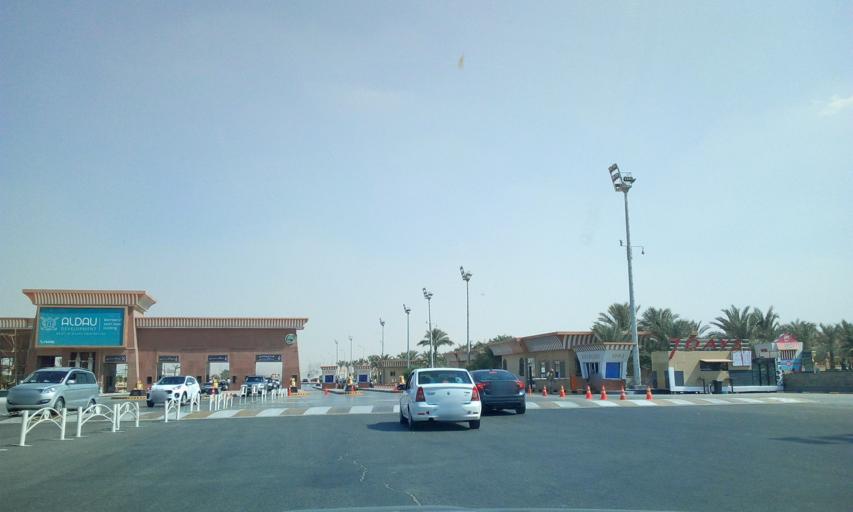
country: EG
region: Muhafazat al Qahirah
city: Halwan
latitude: 29.9630
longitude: 31.4789
